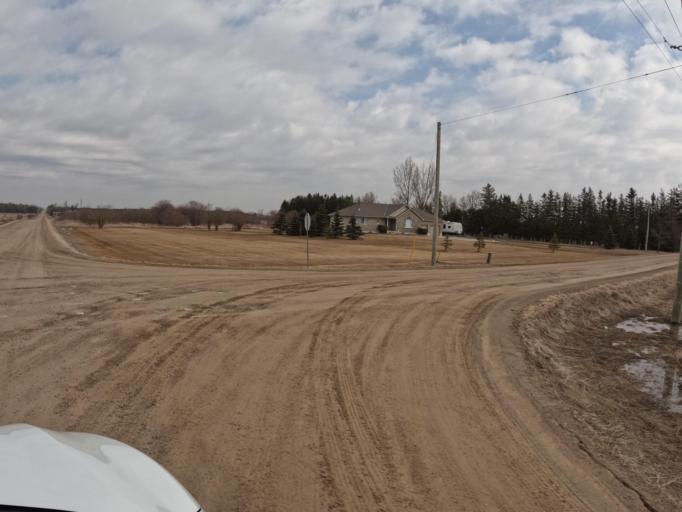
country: CA
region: Ontario
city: Orangeville
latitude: 43.9212
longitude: -80.2181
